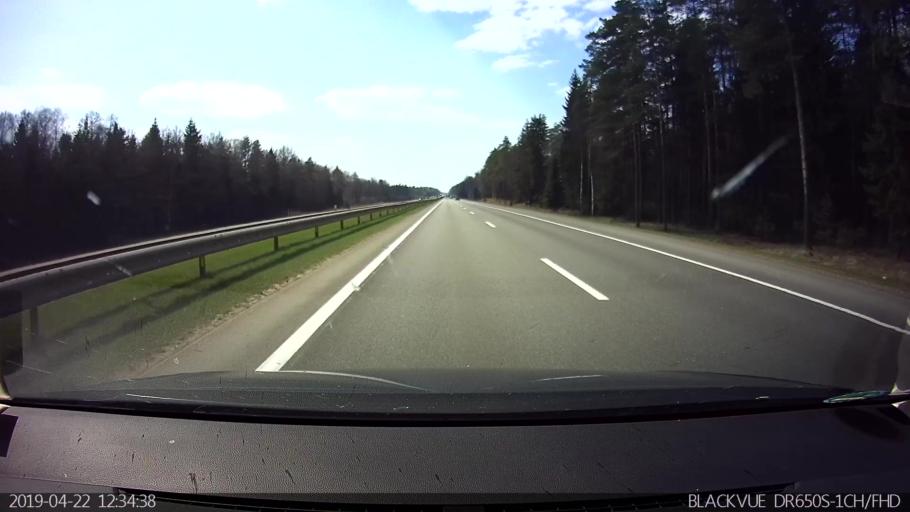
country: BY
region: Minsk
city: Enyerhyetykaw
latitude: 53.5427
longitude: 26.9206
